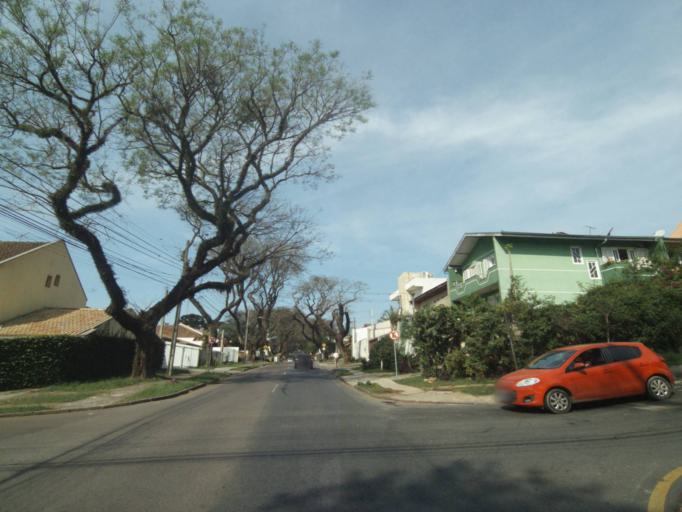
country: BR
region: Parana
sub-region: Curitiba
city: Curitiba
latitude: -25.4606
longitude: -49.3153
